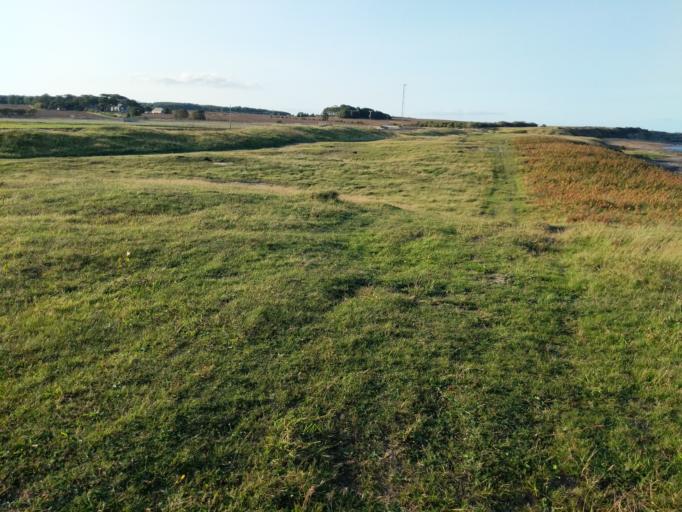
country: GB
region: England
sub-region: Northumberland
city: Lynemouth
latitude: 55.2169
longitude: -1.5287
